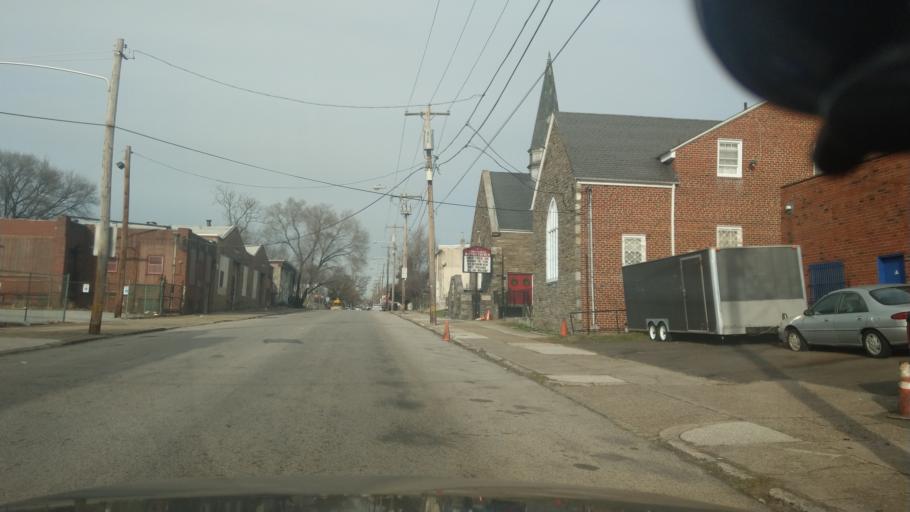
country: US
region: Pennsylvania
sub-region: Montgomery County
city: Wyncote
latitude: 40.0477
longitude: -75.1556
